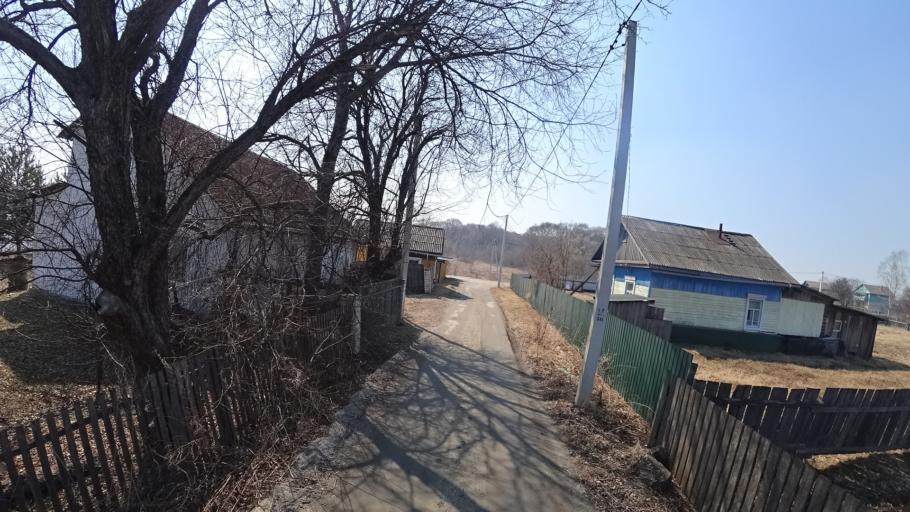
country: RU
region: Amur
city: Novobureyskiy
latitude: 49.7763
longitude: 129.8497
